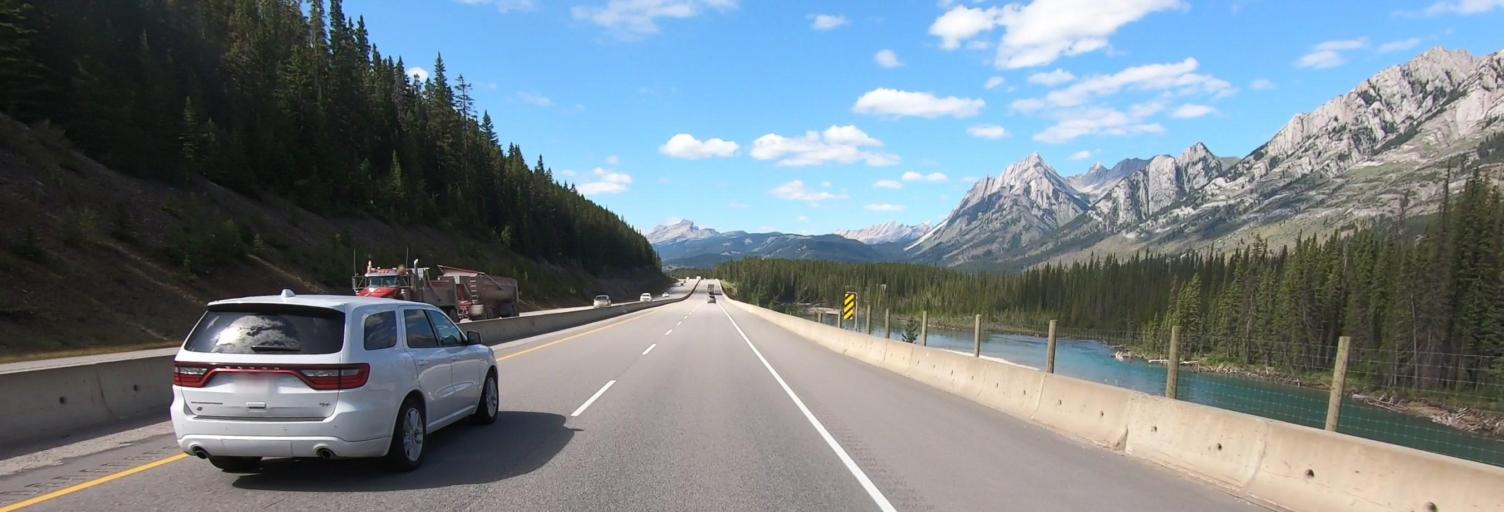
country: CA
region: Alberta
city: Banff
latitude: 51.1803
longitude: -115.7437
